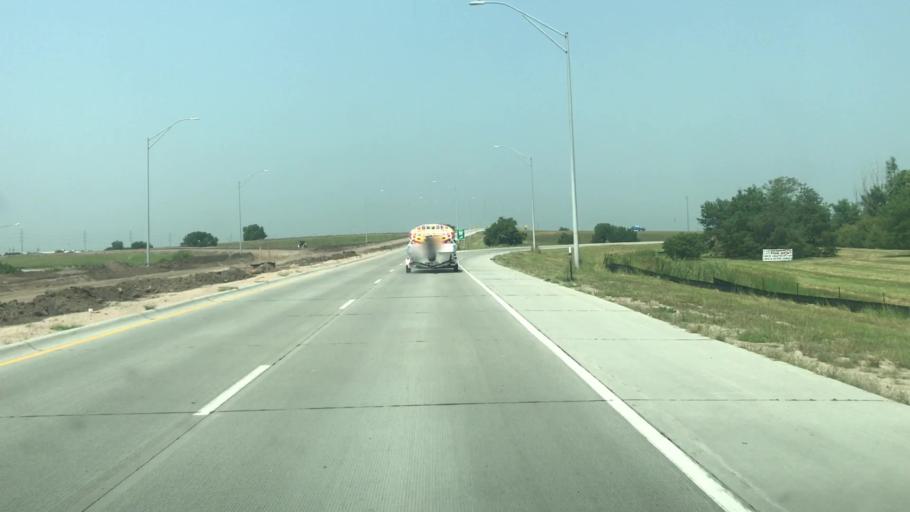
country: US
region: Nebraska
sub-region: Hall County
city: Grand Island
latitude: 40.9493
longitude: -98.3839
